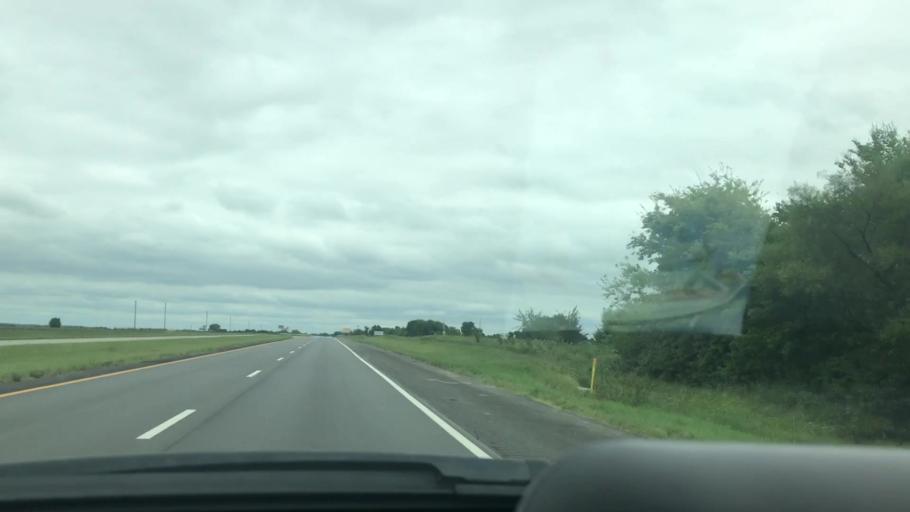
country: US
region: Oklahoma
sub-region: Mayes County
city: Pryor
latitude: 36.4502
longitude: -95.2664
